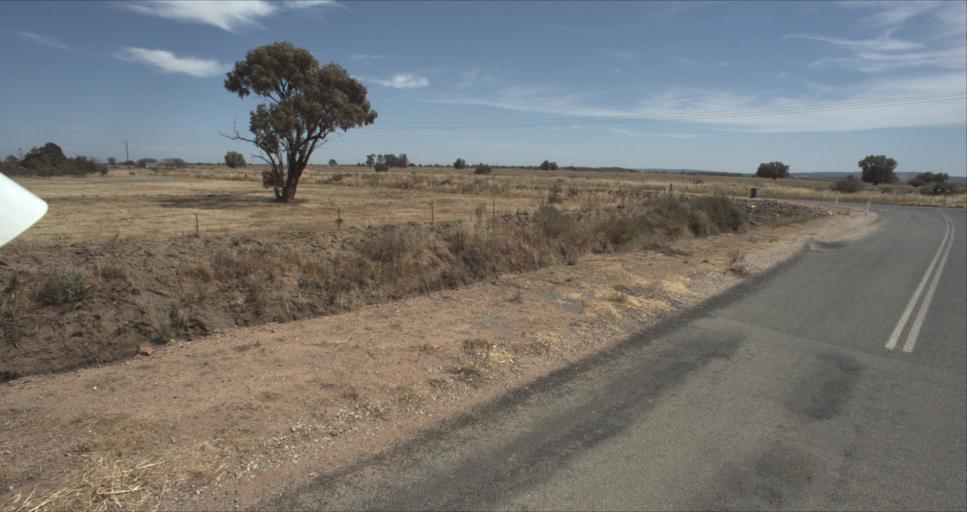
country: AU
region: New South Wales
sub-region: Leeton
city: Leeton
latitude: -34.5582
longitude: 146.4585
